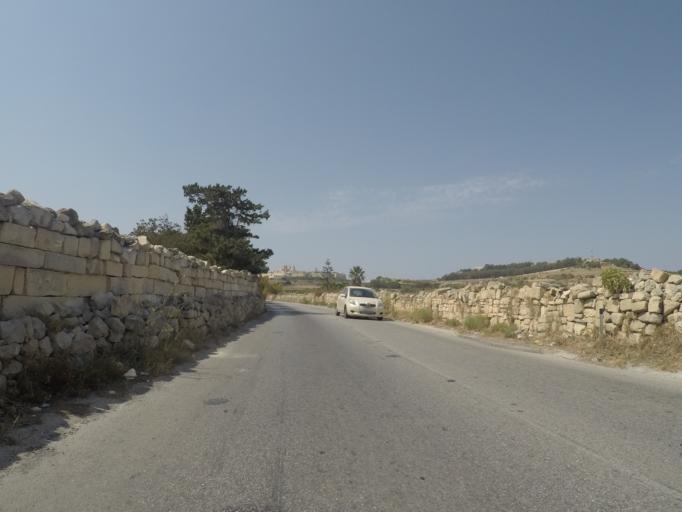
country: MT
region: L-Imtarfa
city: Imtarfa
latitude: 35.8976
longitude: 14.4120
